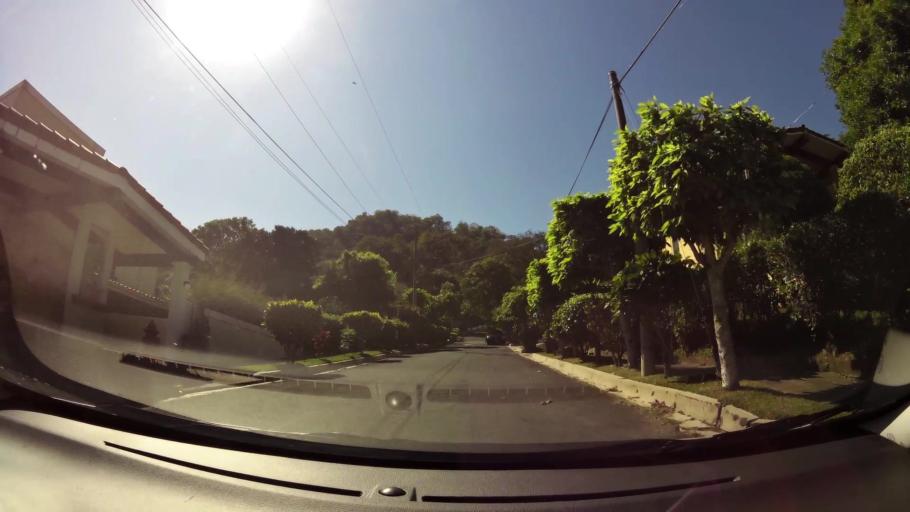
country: SV
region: La Libertad
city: Santa Tecla
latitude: 13.6661
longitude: -89.2893
